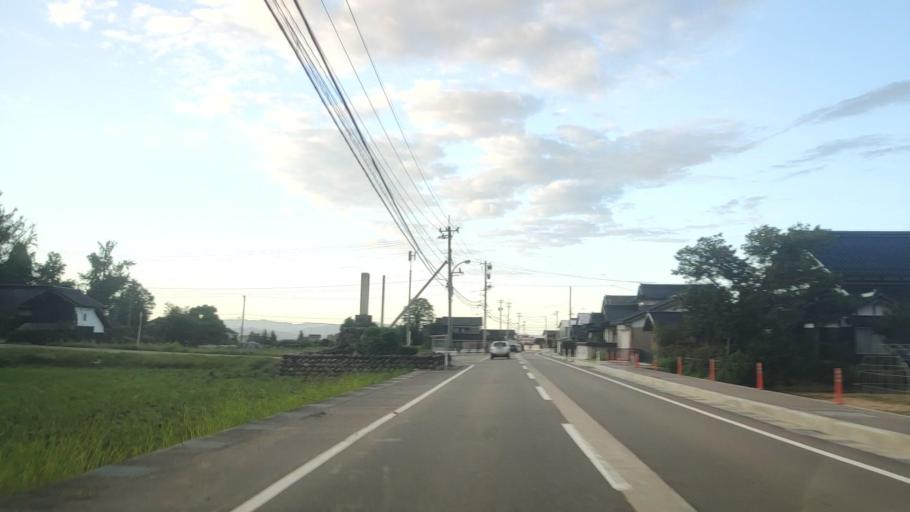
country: JP
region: Toyama
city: Nanto-shi
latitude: 36.6103
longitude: 136.8900
